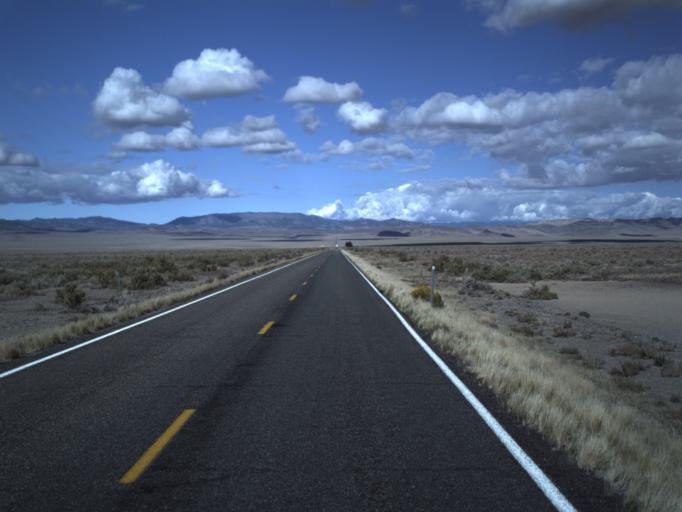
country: US
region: Utah
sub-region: Beaver County
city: Milford
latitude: 38.5267
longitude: -113.6667
